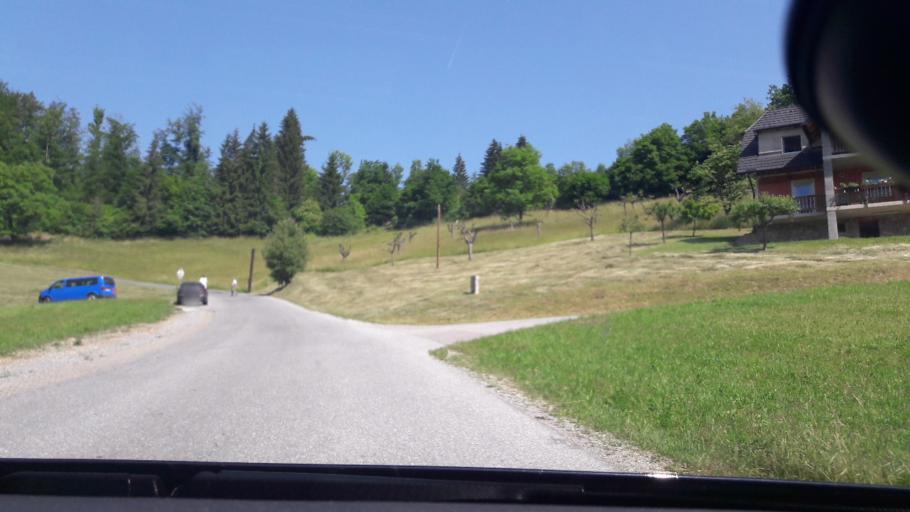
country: AT
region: Styria
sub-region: Politischer Bezirk Voitsberg
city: Sodingberg
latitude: 47.1111
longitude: 15.1602
